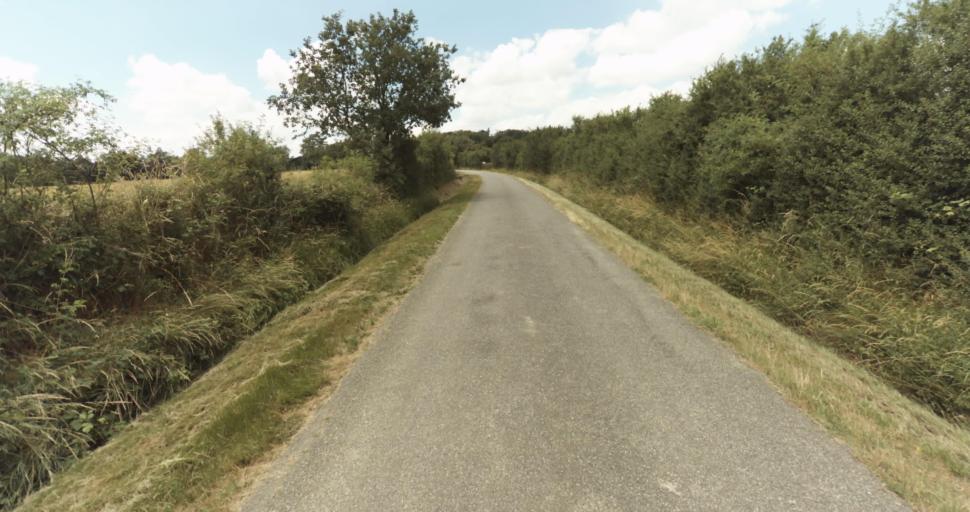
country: FR
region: Midi-Pyrenees
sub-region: Departement de la Haute-Garonne
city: Fontenilles
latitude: 43.5510
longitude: 1.1678
